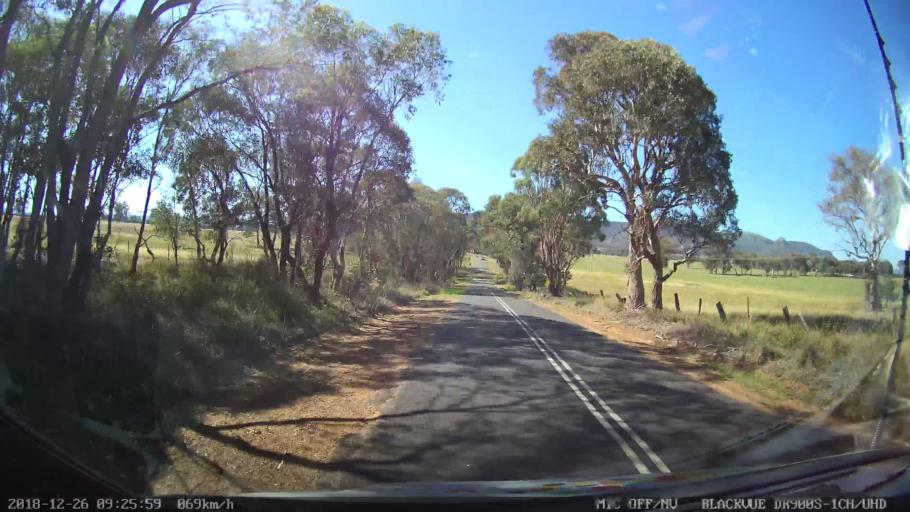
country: AU
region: New South Wales
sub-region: Mid-Western Regional
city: Kandos
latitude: -32.8252
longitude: 150.0061
